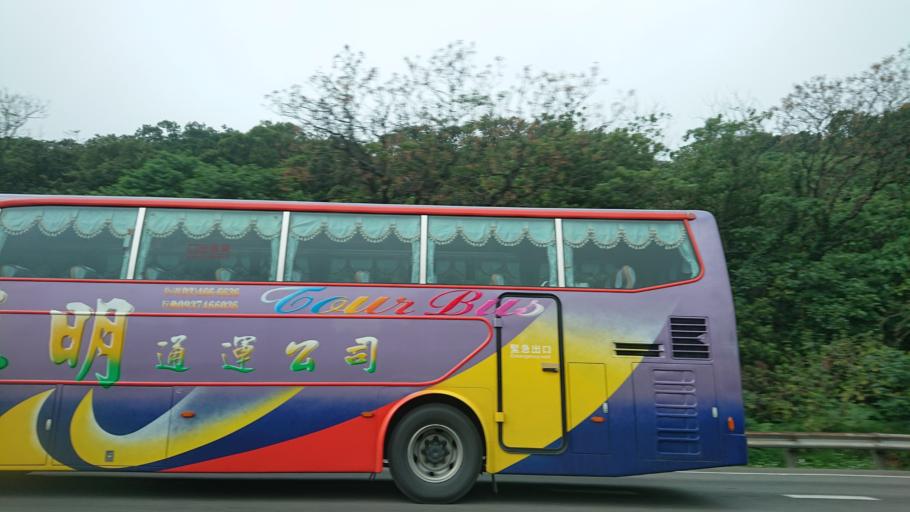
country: TW
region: Taiwan
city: Daxi
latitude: 24.9173
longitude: 121.2955
